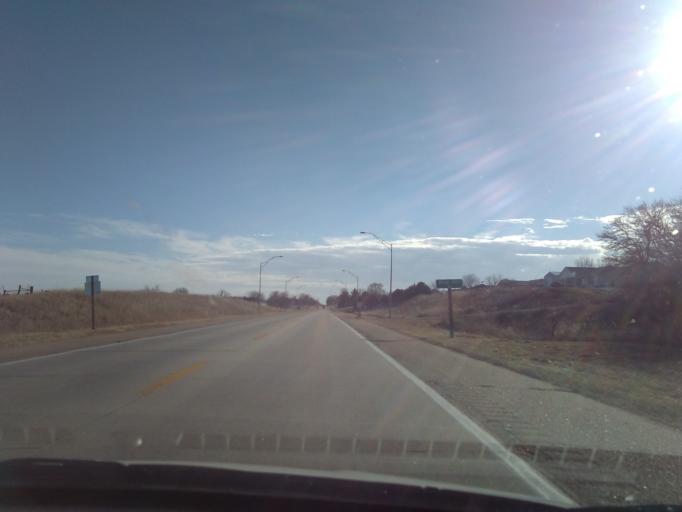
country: US
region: Nebraska
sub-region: Adams County
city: Hastings
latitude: 40.3434
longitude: -98.4439
